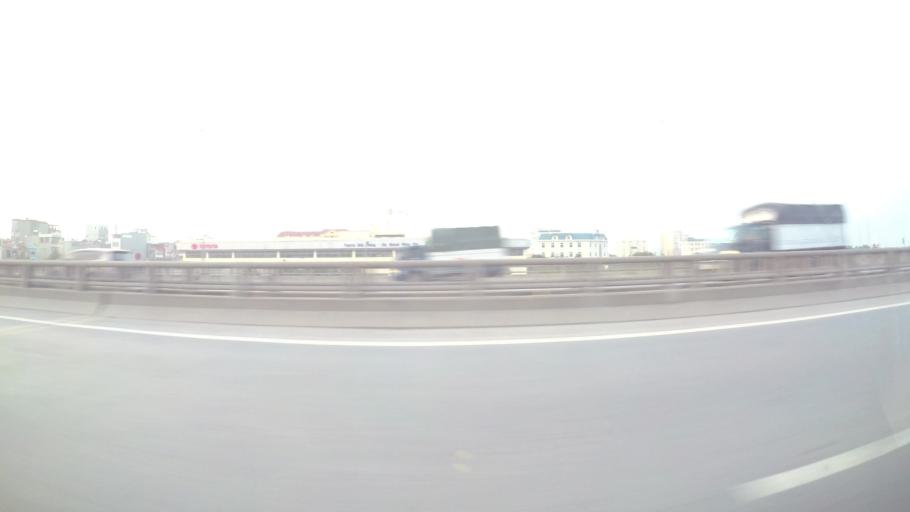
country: VN
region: Ha Noi
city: Van Dien
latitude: 20.9657
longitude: 105.8464
